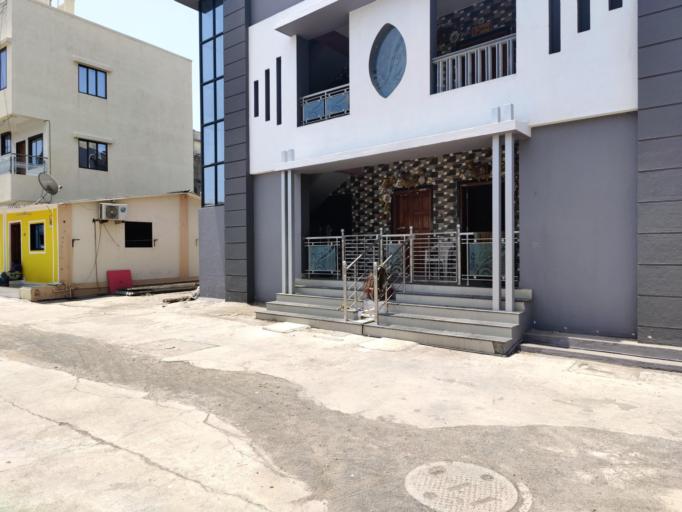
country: IN
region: Daman and Diu
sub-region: Daman District
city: Daman
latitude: 20.4047
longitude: 72.8296
